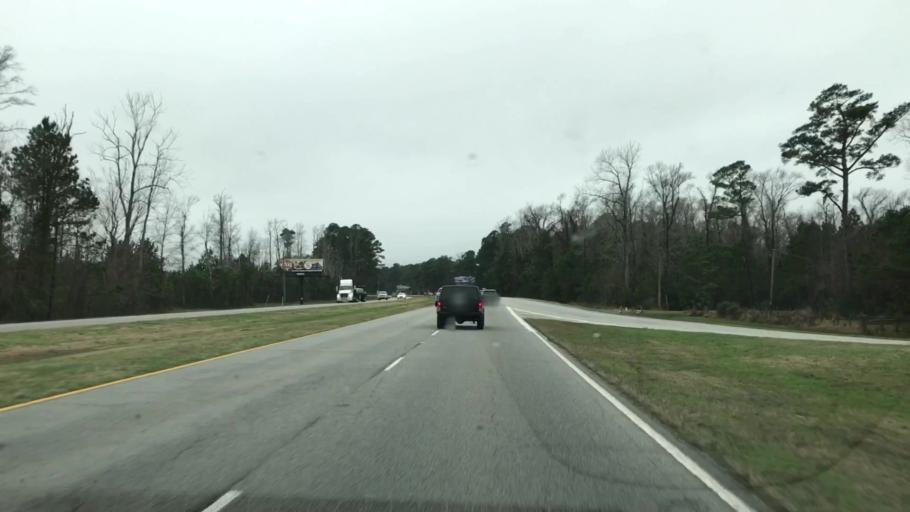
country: US
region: South Carolina
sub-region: Horry County
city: Myrtle Beach
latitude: 33.7384
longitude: -78.8532
